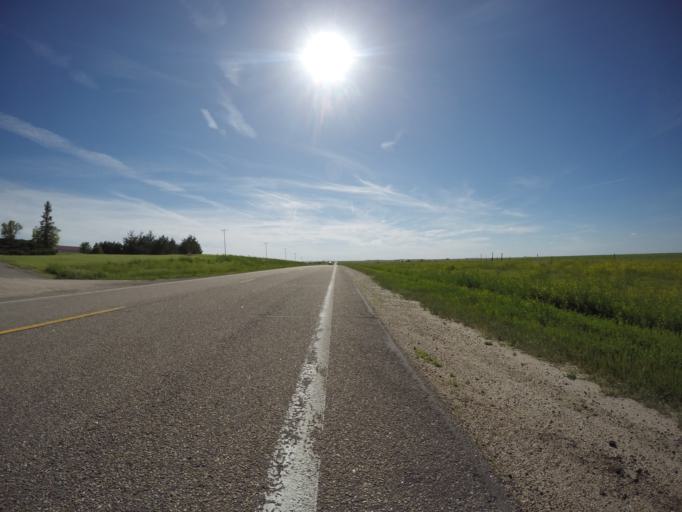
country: US
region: Kansas
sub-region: Cheyenne County
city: Saint Francis
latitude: 39.7566
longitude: -102.0211
